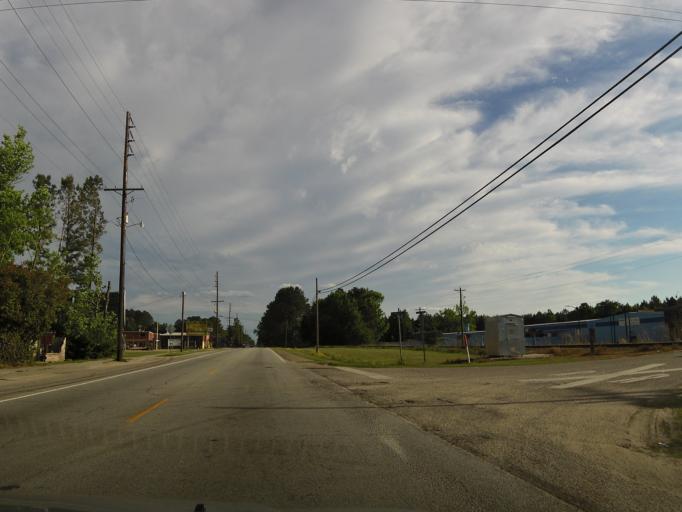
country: US
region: South Carolina
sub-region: Hampton County
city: Estill
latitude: 32.7470
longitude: -81.2415
